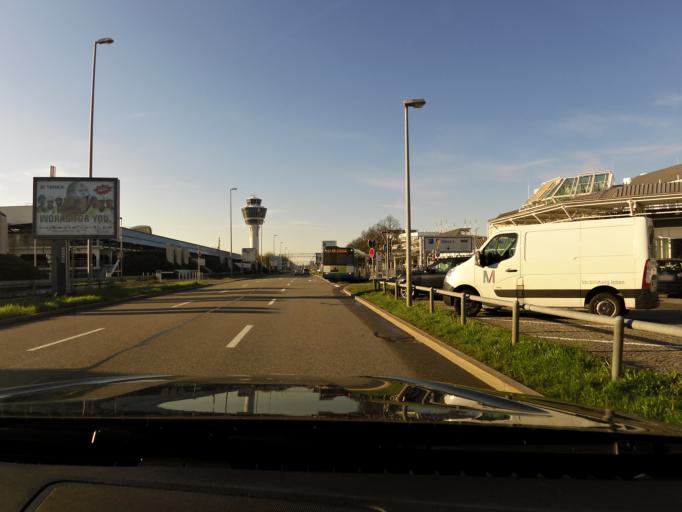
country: DE
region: Bavaria
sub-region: Upper Bavaria
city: Hallbergmoos
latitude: 48.3572
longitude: 11.7846
